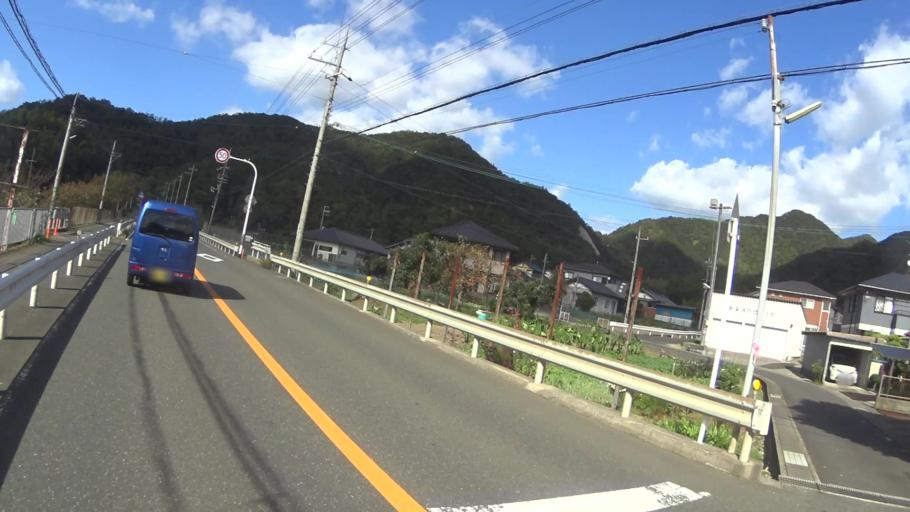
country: JP
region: Kyoto
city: Maizuru
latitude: 35.5000
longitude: 135.4043
